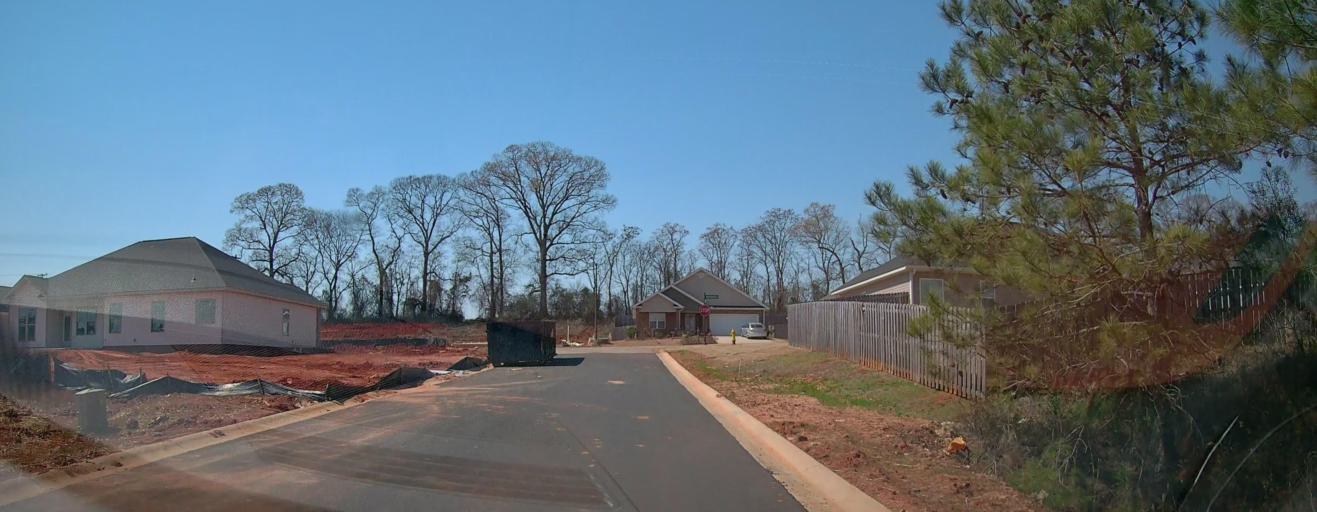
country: US
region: Georgia
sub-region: Peach County
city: Byron
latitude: 32.6079
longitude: -83.7660
